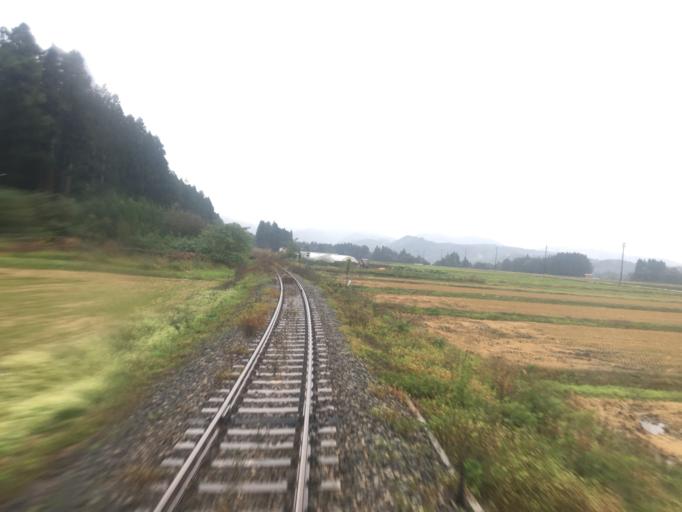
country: JP
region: Yamagata
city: Shinjo
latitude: 38.7023
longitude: 140.3245
